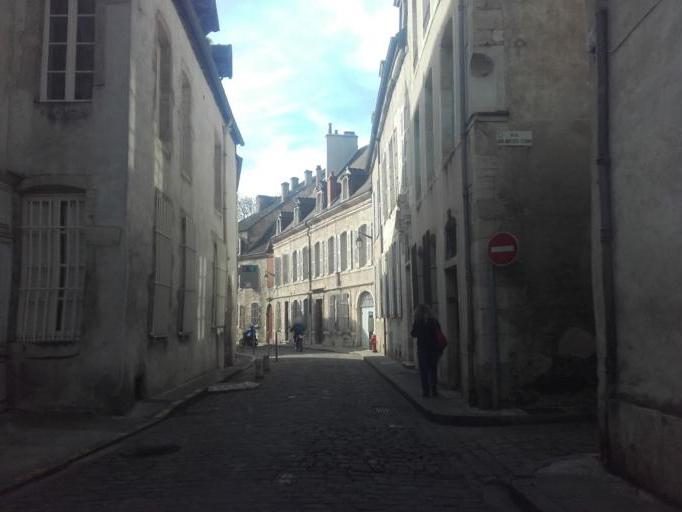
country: FR
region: Bourgogne
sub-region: Departement de la Cote-d'Or
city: Beaune
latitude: 47.0250
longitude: 4.8375
